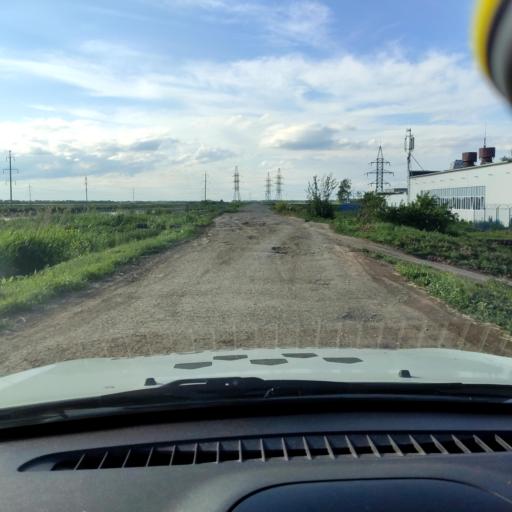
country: RU
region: Samara
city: Tol'yatti
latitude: 53.5916
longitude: 49.4392
